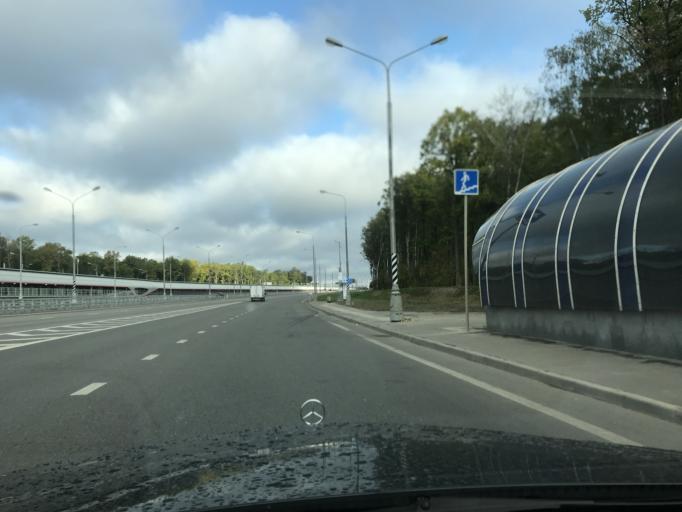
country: RU
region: Moskovskaya
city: Kommunarka
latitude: 55.5759
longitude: 37.4517
